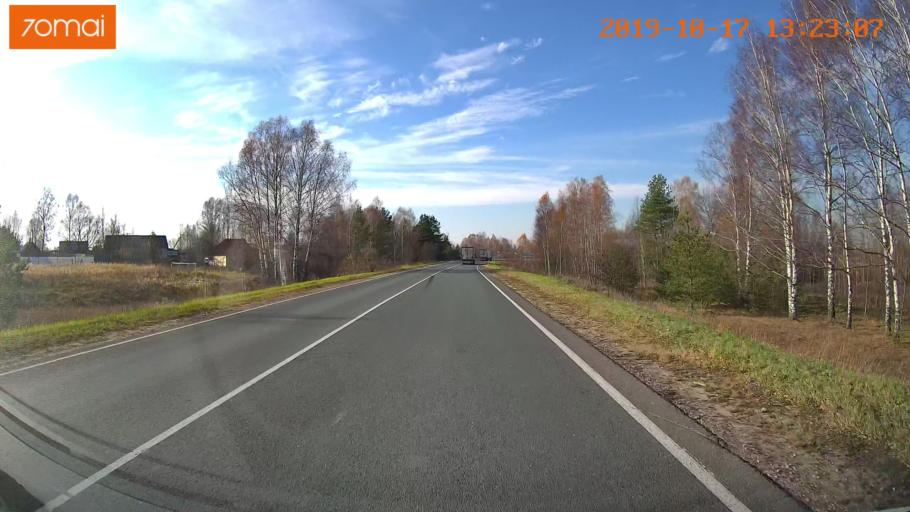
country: RU
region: Rjazan
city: Gus'-Zheleznyy
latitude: 55.0879
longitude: 40.9857
